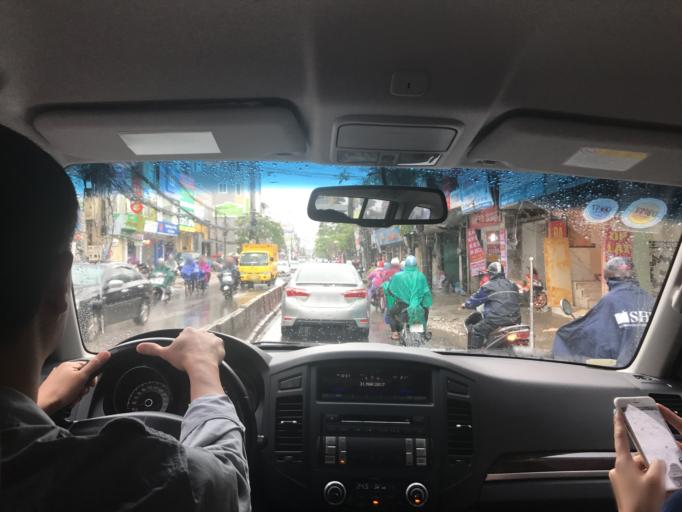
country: VN
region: Ha Noi
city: Dong Da
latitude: 21.0010
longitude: 105.8280
